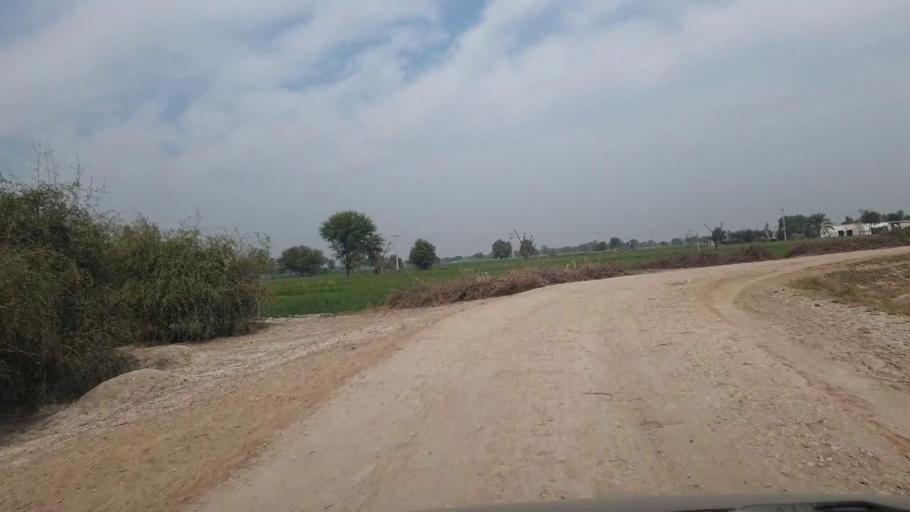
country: PK
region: Sindh
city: Shahdadpur
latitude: 25.9359
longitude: 68.6811
